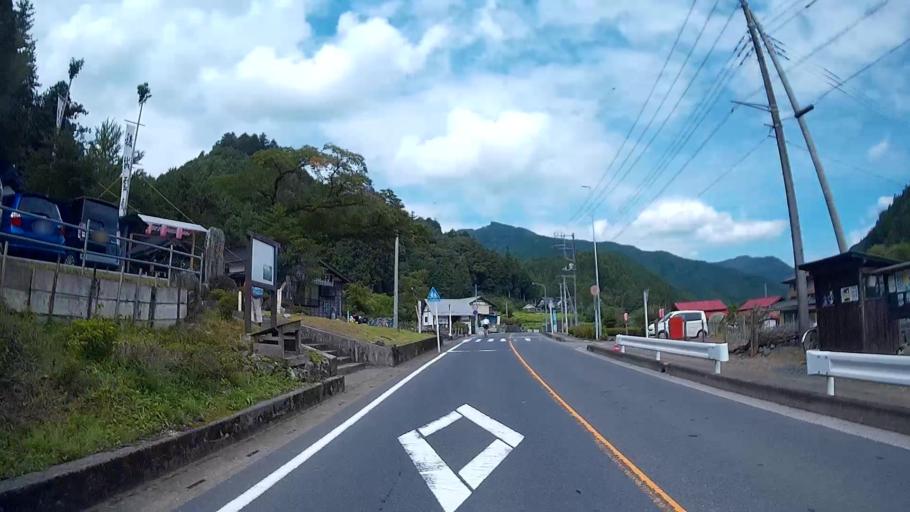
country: JP
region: Tokyo
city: Ome
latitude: 35.8540
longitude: 139.1951
